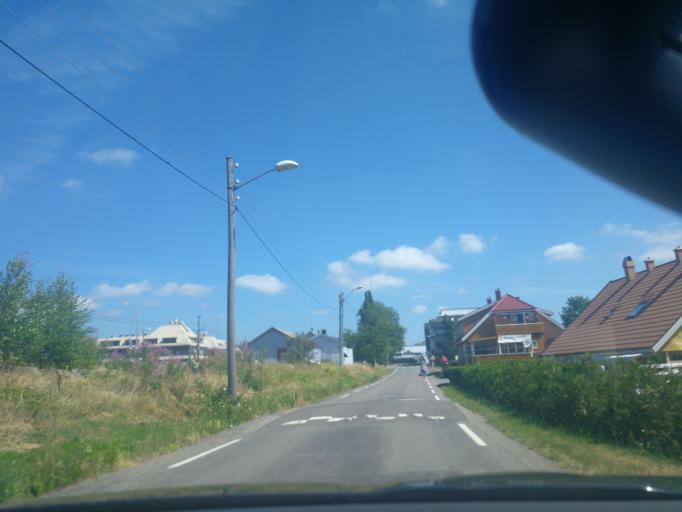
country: NO
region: Vestfold
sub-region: Stokke
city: Stokke
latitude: 59.2203
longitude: 10.2989
